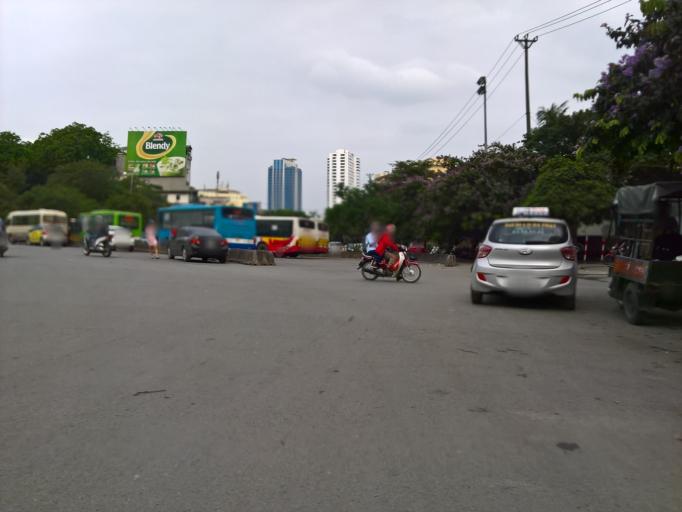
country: VN
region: Ha Noi
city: Cau Giay
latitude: 21.0281
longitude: 105.8050
